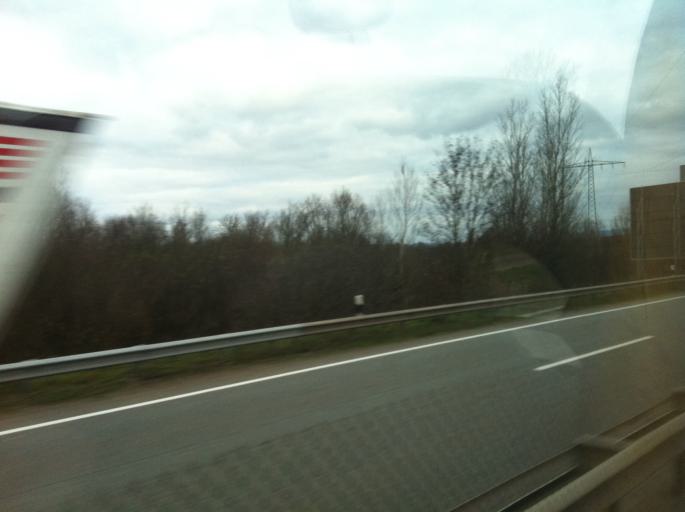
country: DE
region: Rheinland-Pfalz
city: Gensingen
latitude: 49.8887
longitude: 7.9383
